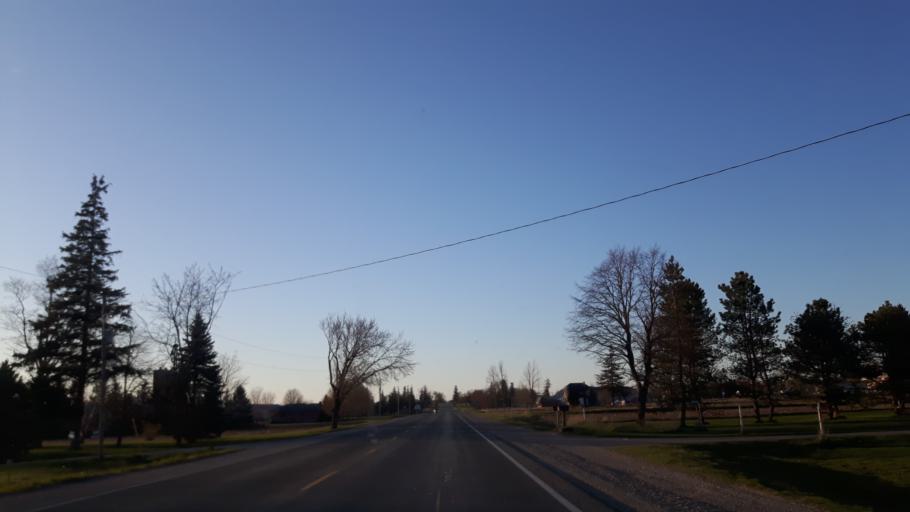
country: CA
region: Ontario
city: Bluewater
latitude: 43.5754
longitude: -81.5277
